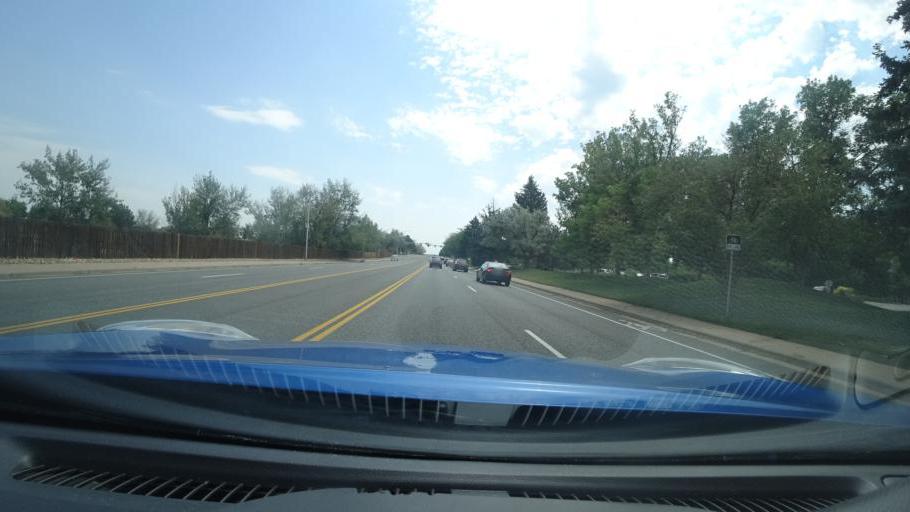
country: US
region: Colorado
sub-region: Adams County
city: Aurora
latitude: 39.6675
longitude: -104.8240
